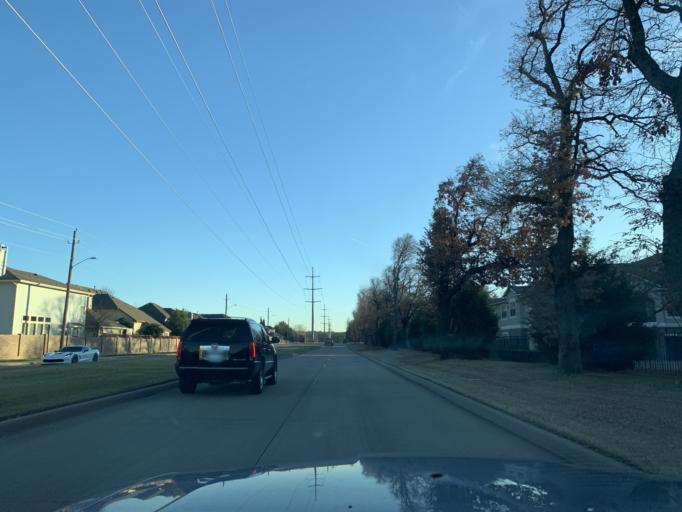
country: US
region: Texas
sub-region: Tarrant County
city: Euless
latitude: 32.8724
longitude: -97.0959
